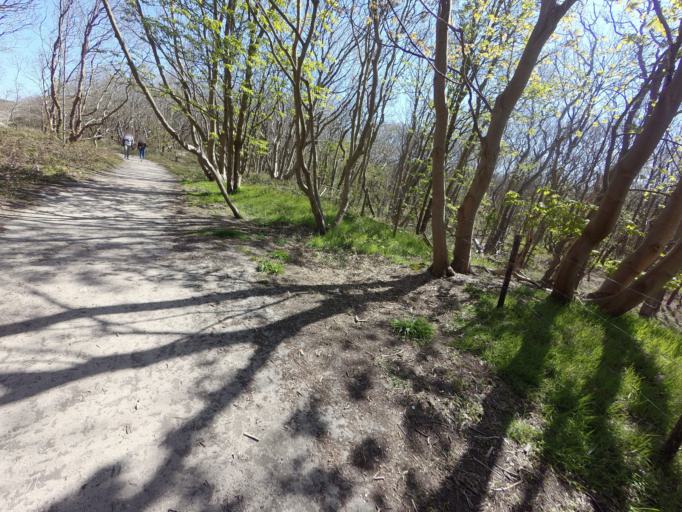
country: NL
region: Zeeland
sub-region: Gemeente Middelburg
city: Middelburg
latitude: 51.5683
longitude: 3.5070
